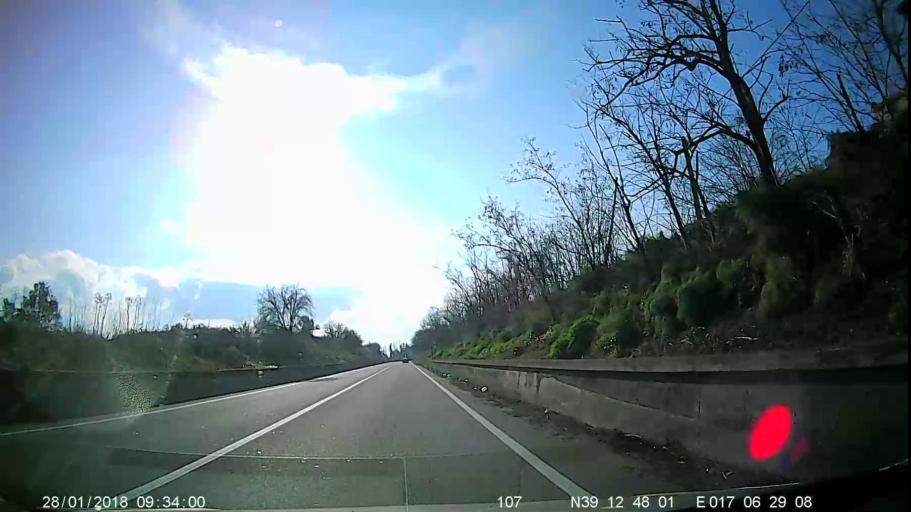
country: IT
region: Calabria
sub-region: Provincia di Crotone
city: Tronca
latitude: 39.2129
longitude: 17.1083
